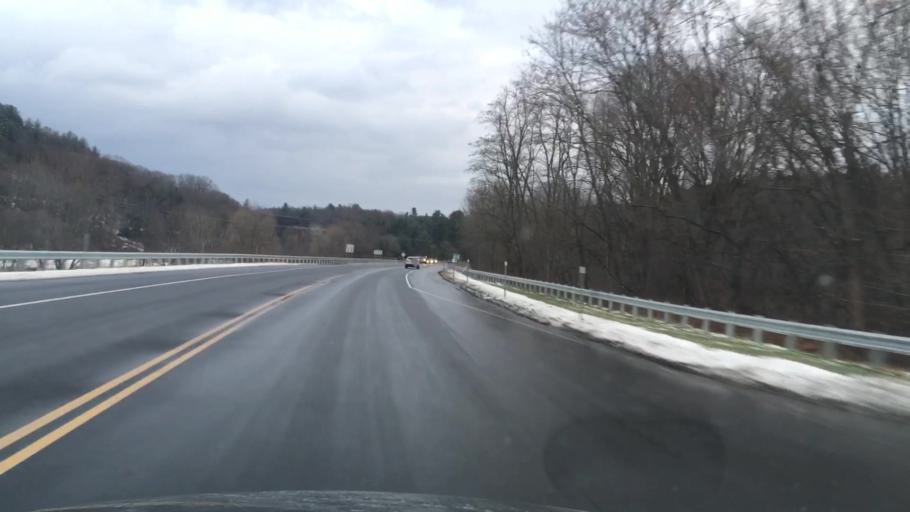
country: US
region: New Hampshire
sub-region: Sullivan County
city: Claremont
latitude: 43.3987
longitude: -72.3927
